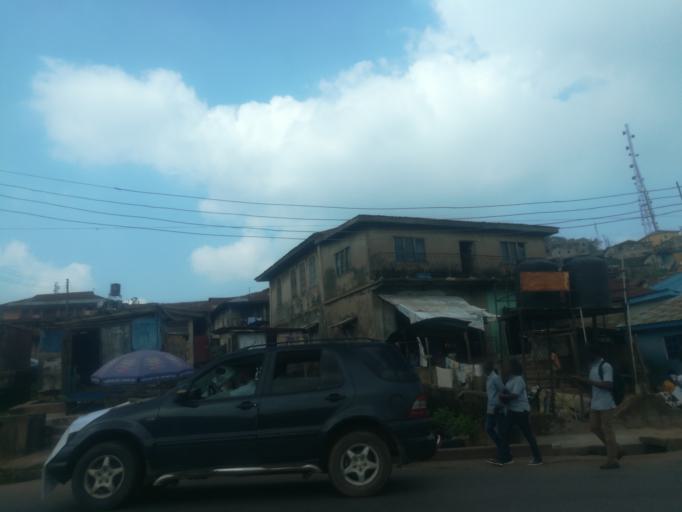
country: NG
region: Oyo
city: Ibadan
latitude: 7.3863
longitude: 3.8999
